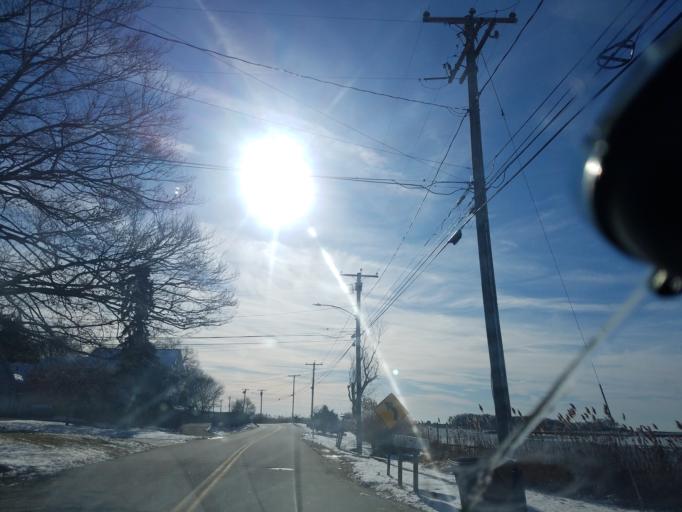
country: US
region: Connecticut
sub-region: New London County
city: Niantic
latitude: 41.3064
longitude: -72.2177
